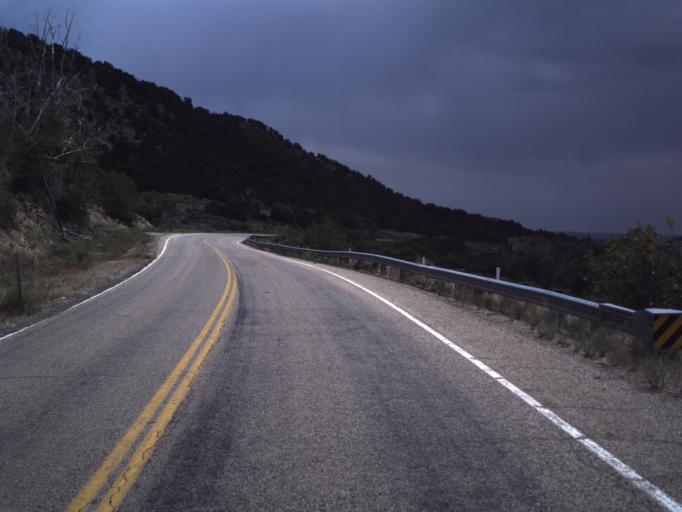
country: US
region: Utah
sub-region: Duchesne County
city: Duchesne
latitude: 40.4169
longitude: -110.7849
